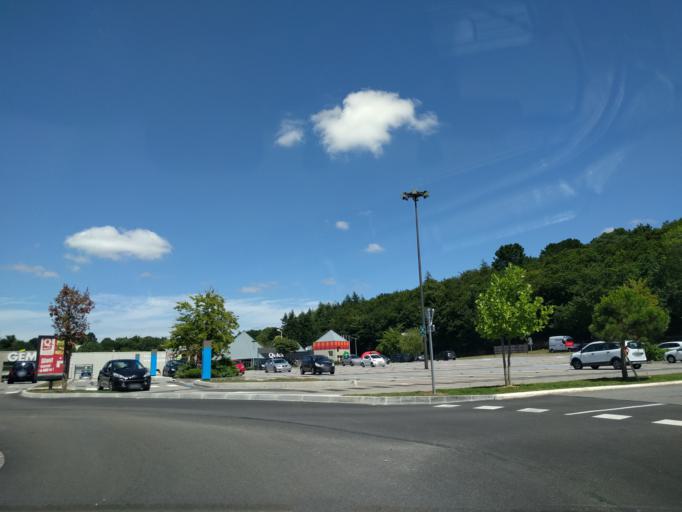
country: FR
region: Brittany
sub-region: Departement du Finistere
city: Quimper
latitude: 47.9756
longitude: -4.0935
